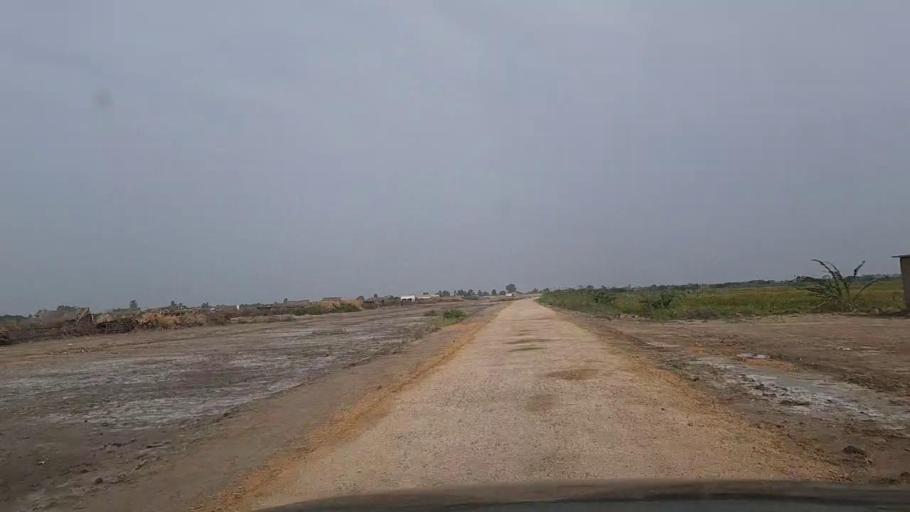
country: PK
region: Sindh
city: Thatta
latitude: 24.7470
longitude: 67.8264
